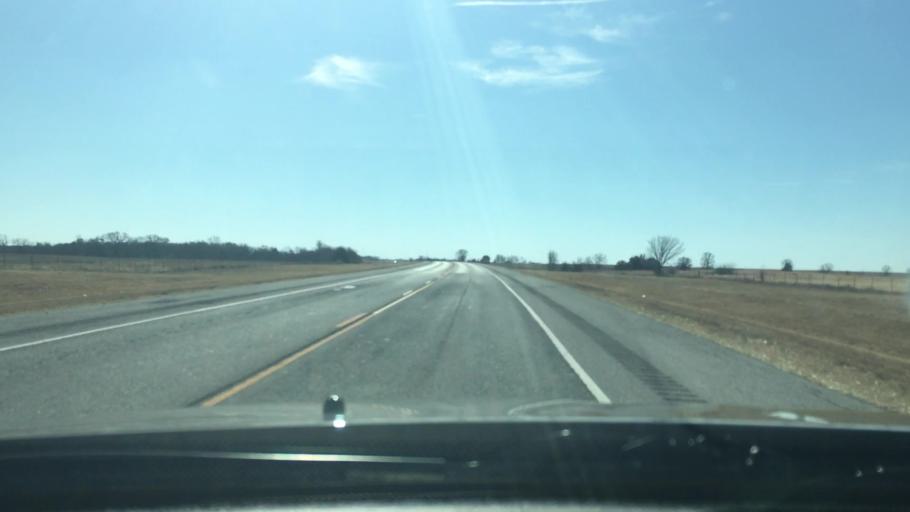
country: US
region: Oklahoma
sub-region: Stephens County
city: Meridian
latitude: 34.4015
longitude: -97.9742
